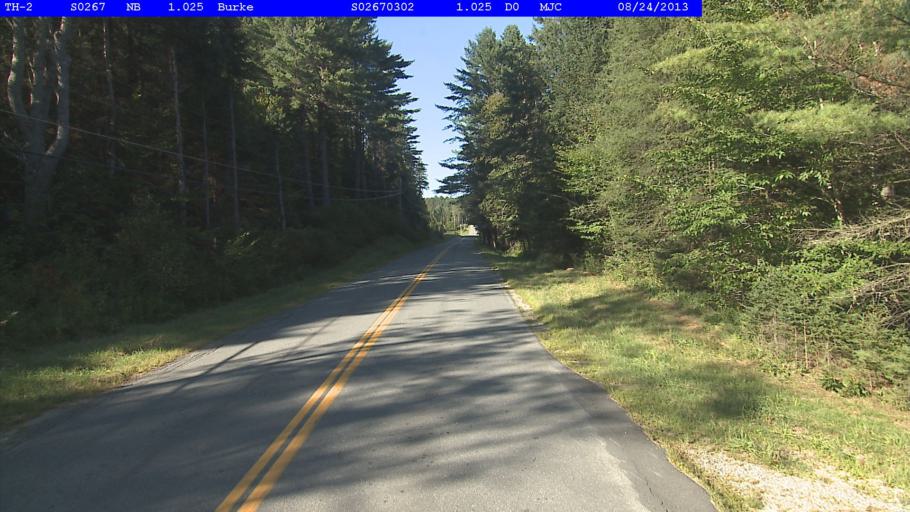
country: US
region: Vermont
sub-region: Caledonia County
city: Lyndonville
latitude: 44.6013
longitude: -71.9405
